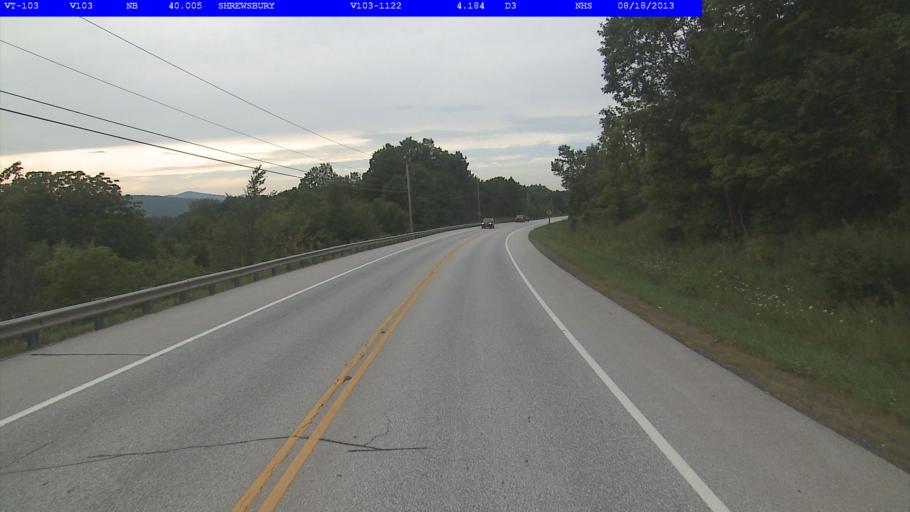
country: US
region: Vermont
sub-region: Rutland County
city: Rutland
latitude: 43.5231
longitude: -72.9303
